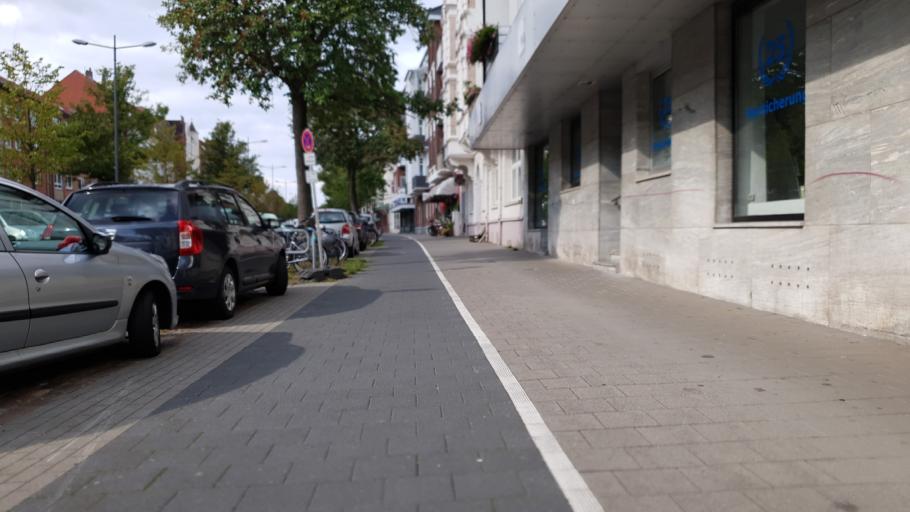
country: DE
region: Schleswig-Holstein
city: Kiel
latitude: 54.3258
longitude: 10.1211
